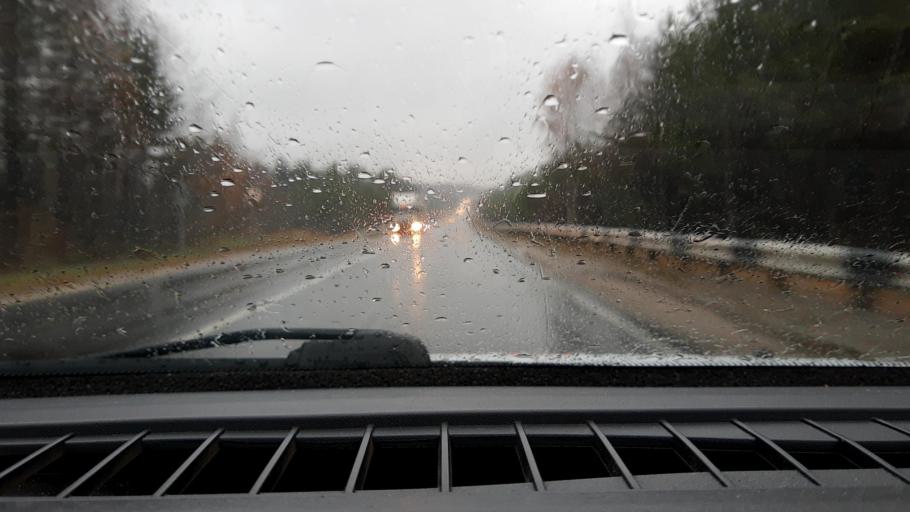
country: RU
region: Nizjnij Novgorod
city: Sitniki
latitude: 56.4730
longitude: 44.0333
